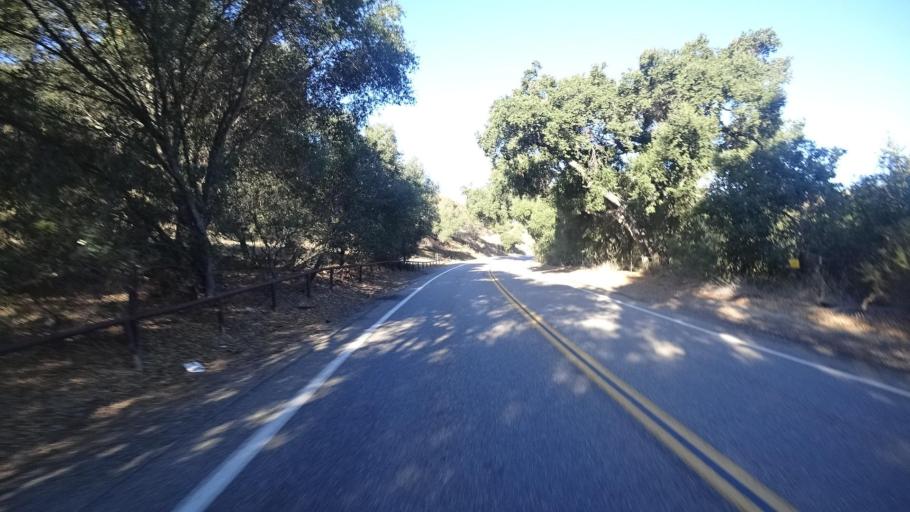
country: US
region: California
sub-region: San Diego County
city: Jamul
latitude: 32.6499
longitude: -116.8639
